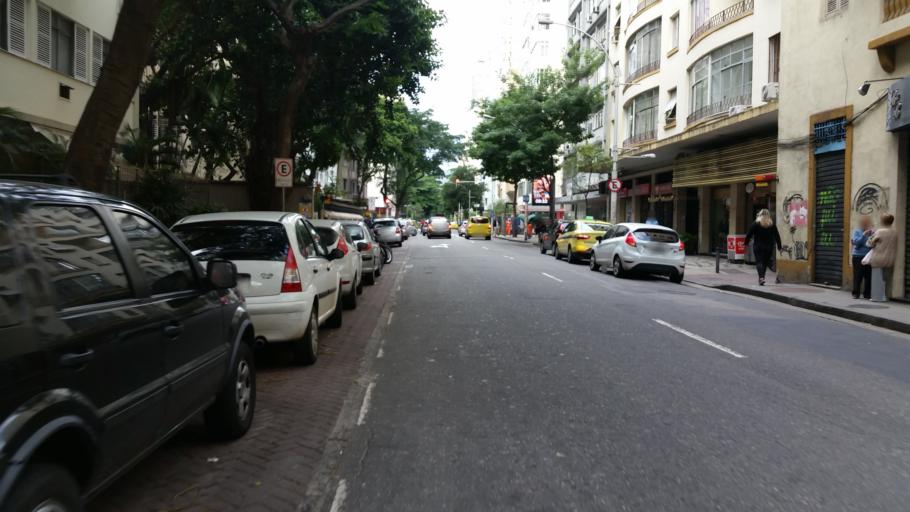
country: BR
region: Rio de Janeiro
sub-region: Rio De Janeiro
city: Rio de Janeiro
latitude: -22.9367
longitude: -43.1774
